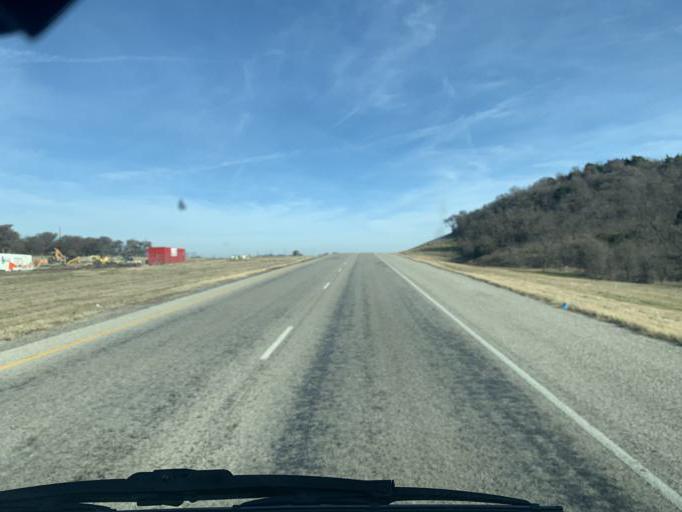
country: US
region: Texas
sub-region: Dallas County
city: Cedar Hill
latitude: 32.6283
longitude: -96.9749
